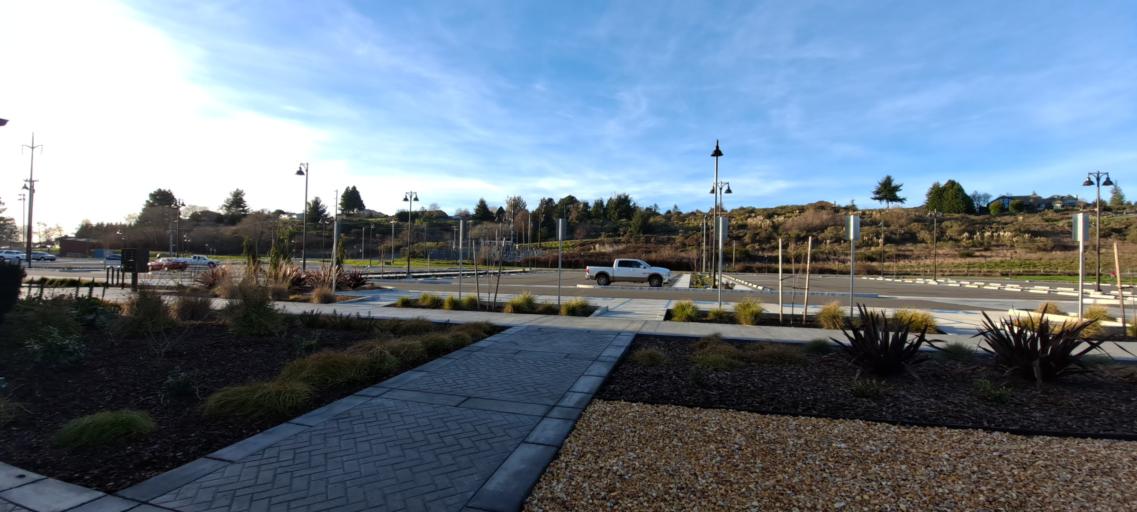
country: US
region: California
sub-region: Humboldt County
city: Fortuna
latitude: 40.5939
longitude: -124.1338
